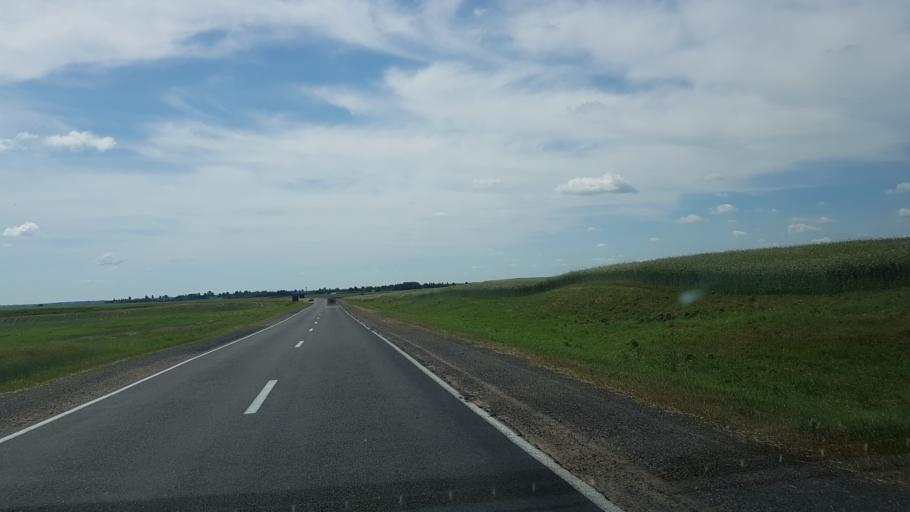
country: BY
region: Vitebsk
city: Dubrowna
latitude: 54.6339
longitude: 30.6634
